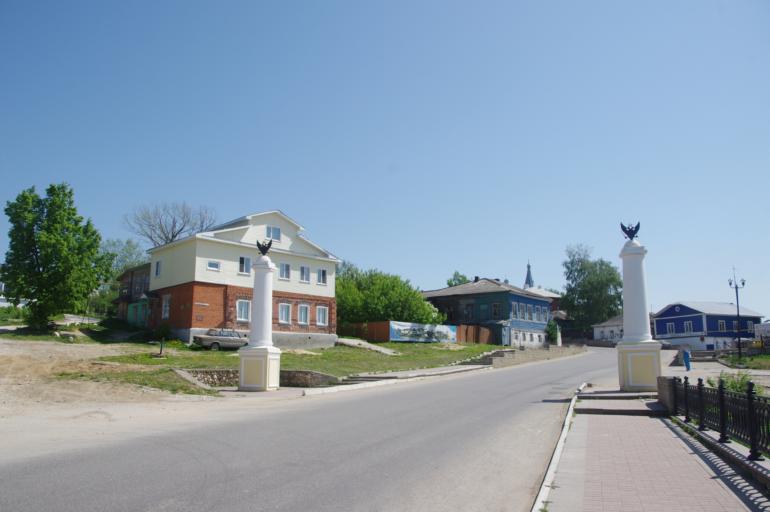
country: RU
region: Rjazan
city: Kasimov
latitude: 54.9371
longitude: 41.3845
